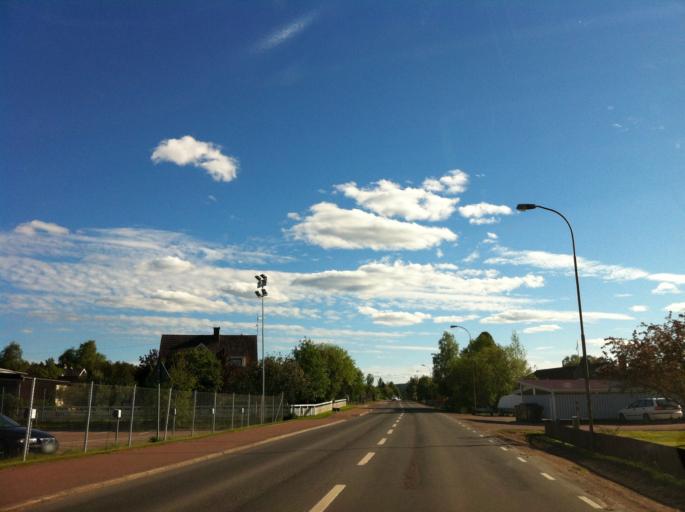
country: SE
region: Dalarna
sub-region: Leksand Municipality
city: Leksand
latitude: 60.7272
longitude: 14.9983
